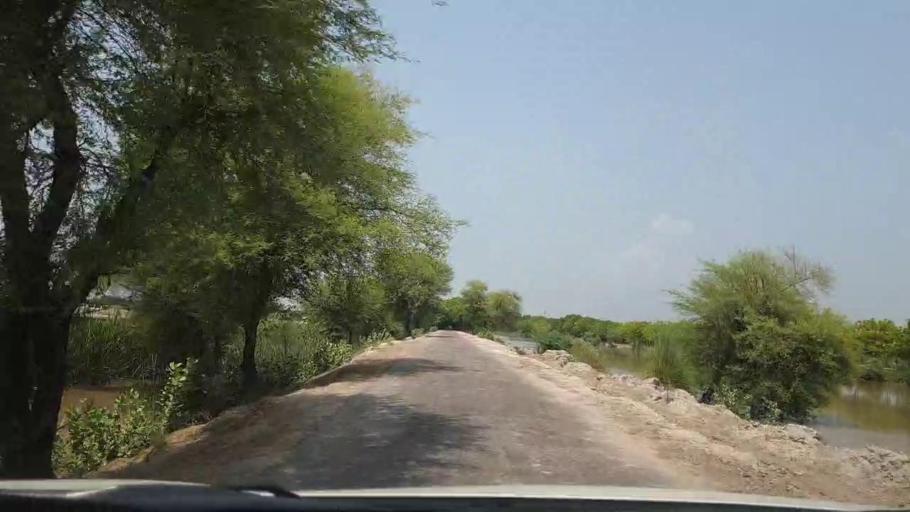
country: PK
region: Sindh
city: Dokri
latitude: 27.3564
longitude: 68.1132
